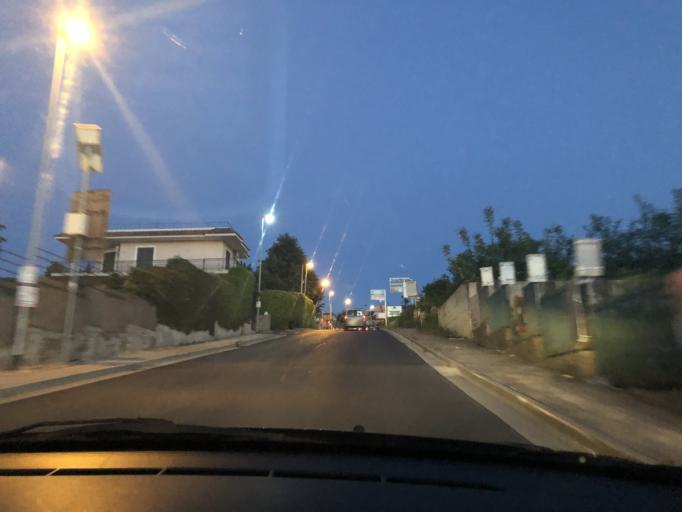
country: IT
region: Campania
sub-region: Provincia di Napoli
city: Torre Caracciolo
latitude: 40.8865
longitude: 14.1815
